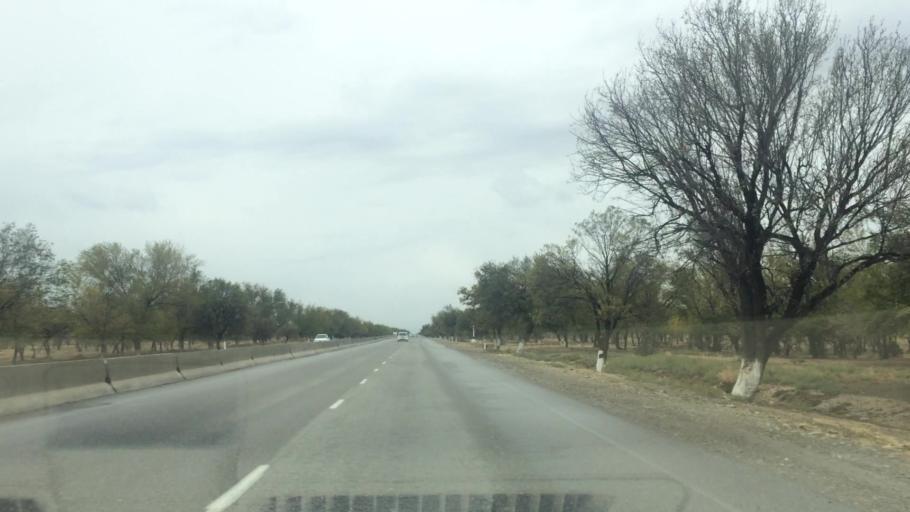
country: UZ
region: Samarqand
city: Bulung'ur
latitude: 39.8285
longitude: 67.4074
